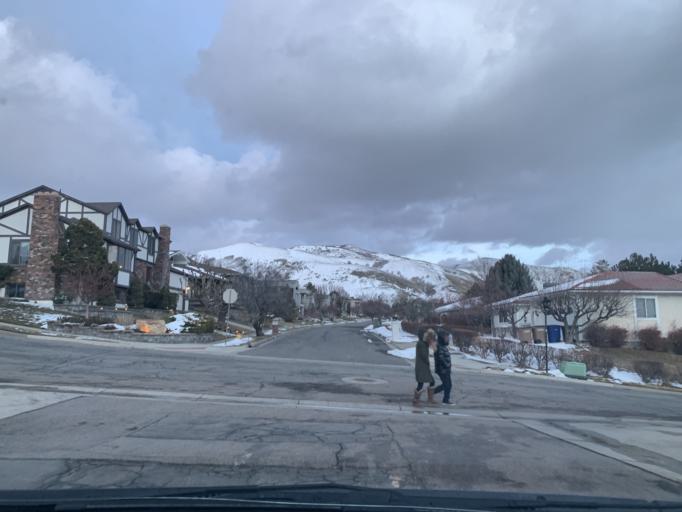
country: US
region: Utah
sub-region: Salt Lake County
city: Salt Lake City
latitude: 40.7821
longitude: -111.8509
